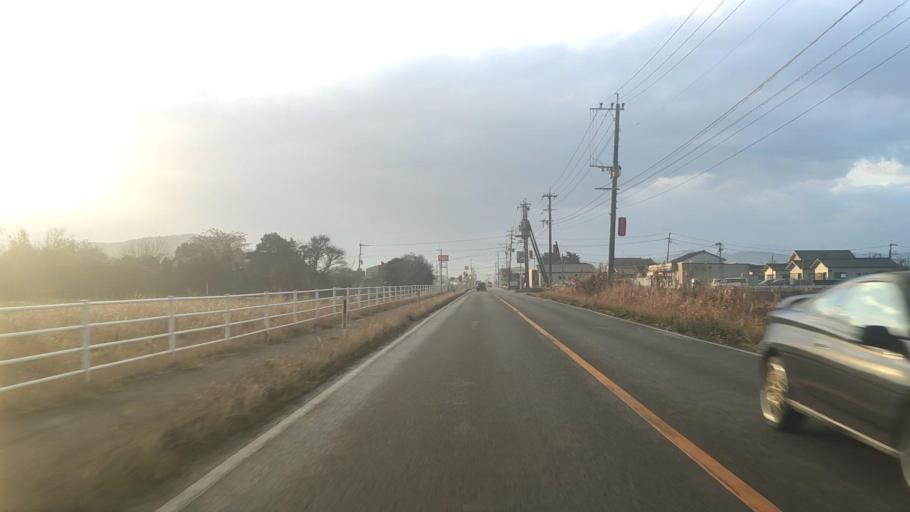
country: JP
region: Kumamoto
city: Uto
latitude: 32.7175
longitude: 130.7720
